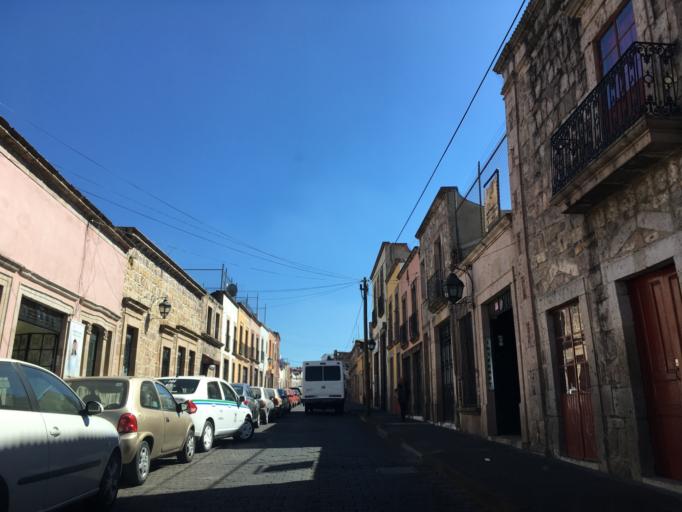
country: MX
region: Michoacan
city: Morelia
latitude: 19.7021
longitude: -101.2010
